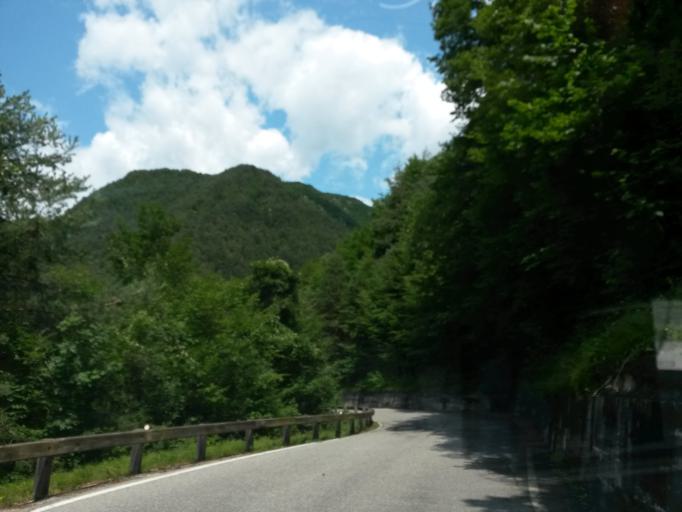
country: IT
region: Lombardy
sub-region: Provincia di Brescia
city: Valvestino
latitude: 45.7339
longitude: 10.6063
